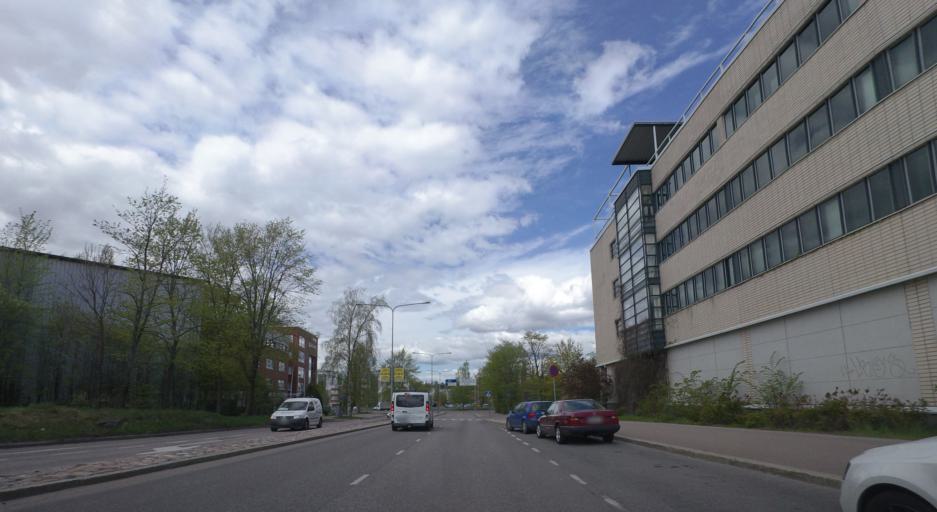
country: FI
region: Uusimaa
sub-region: Helsinki
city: Vantaa
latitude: 60.2479
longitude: 25.0087
